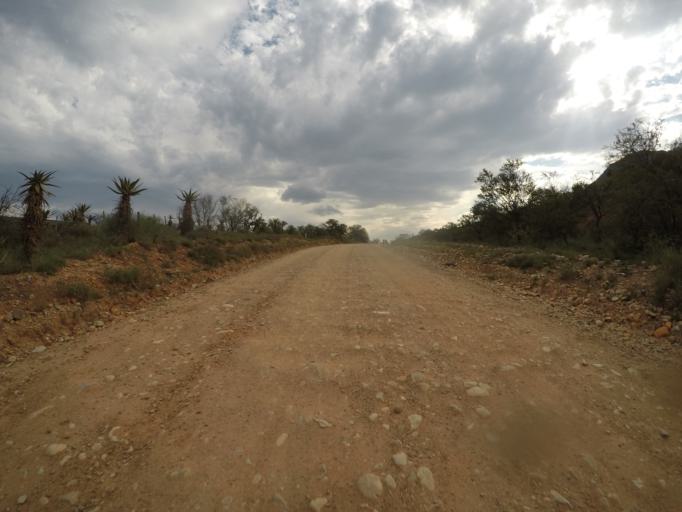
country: ZA
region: Eastern Cape
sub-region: Cacadu District Municipality
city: Kareedouw
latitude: -33.5831
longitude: 24.1633
